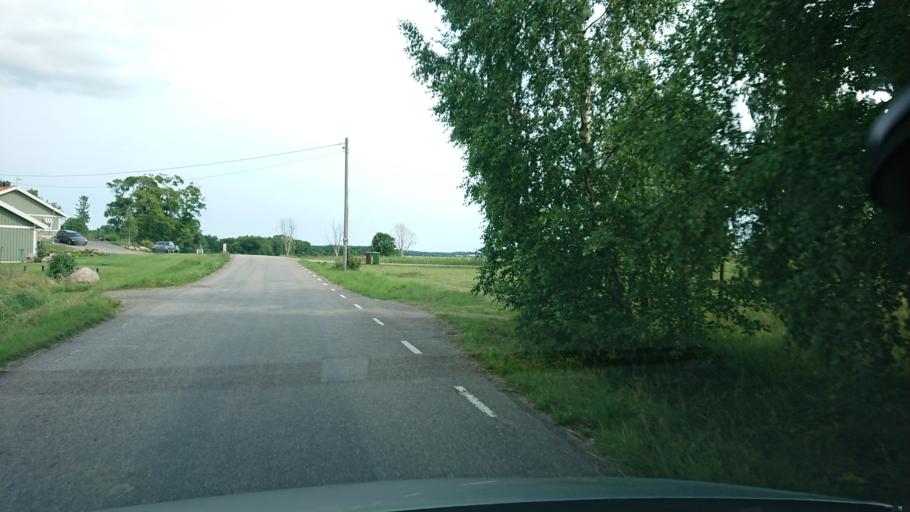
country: SE
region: Uppsala
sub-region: Osthammars Kommun
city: Bjorklinge
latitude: 59.9861
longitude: 17.5550
